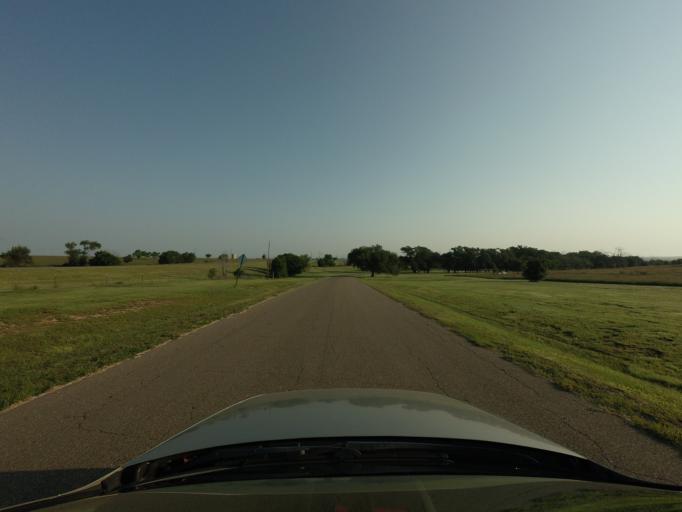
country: US
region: New Mexico
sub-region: Curry County
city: Clovis
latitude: 34.5187
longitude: -103.1959
